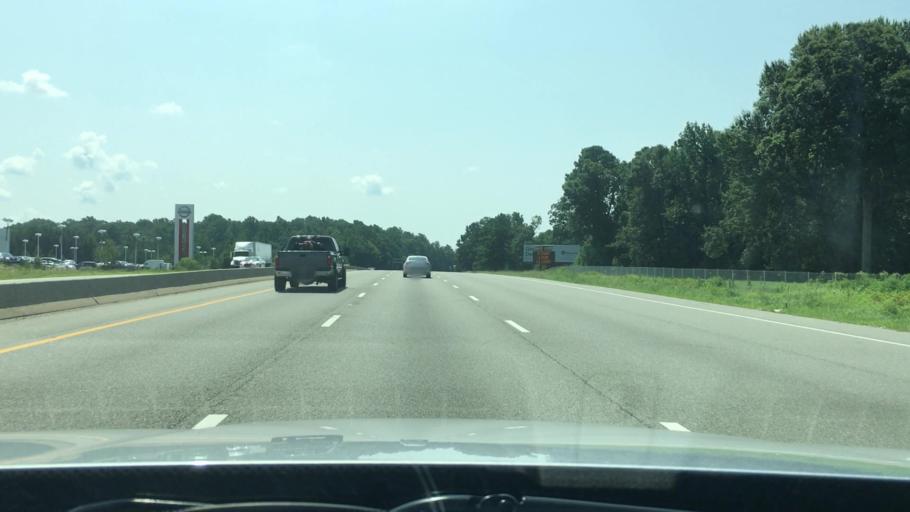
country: US
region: Virginia
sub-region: City of Colonial Heights
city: Colonial Heights
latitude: 37.3059
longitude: -77.3944
